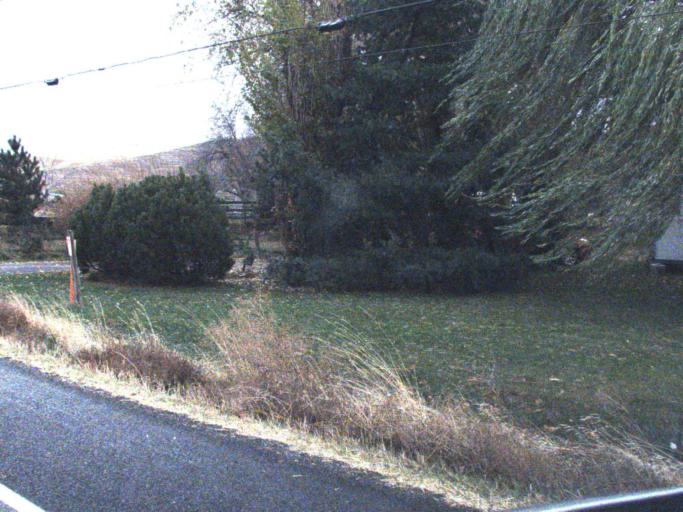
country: US
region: Washington
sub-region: Columbia County
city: Dayton
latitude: 46.2897
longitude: -118.0314
